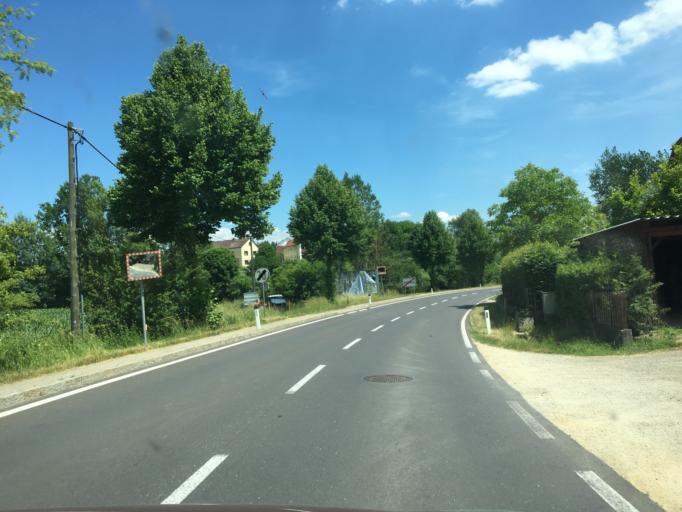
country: AT
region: Upper Austria
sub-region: Politischer Bezirk Urfahr-Umgebung
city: Engerwitzdorf
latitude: 48.3780
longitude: 14.5061
